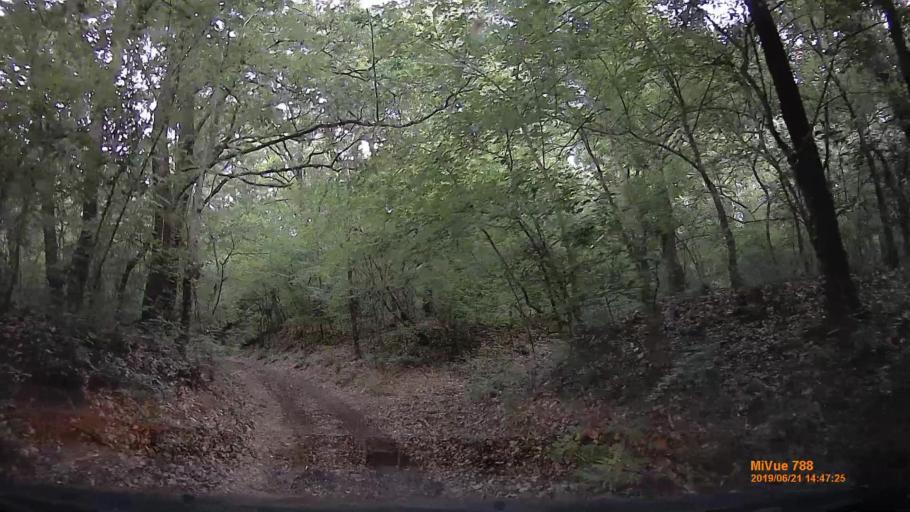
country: HU
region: Baranya
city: Hosszuheteny
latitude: 46.1310
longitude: 18.3085
